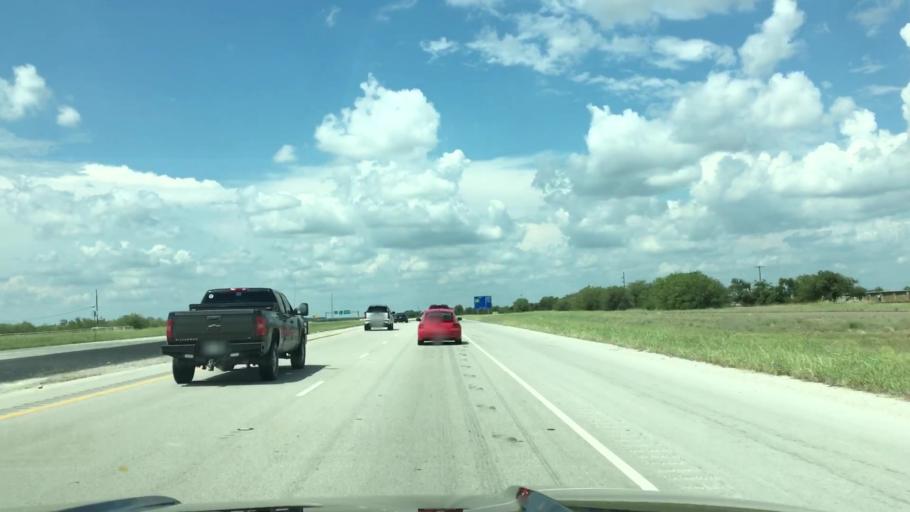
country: US
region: Texas
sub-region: Wise County
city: Rhome
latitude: 33.0365
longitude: -97.4529
